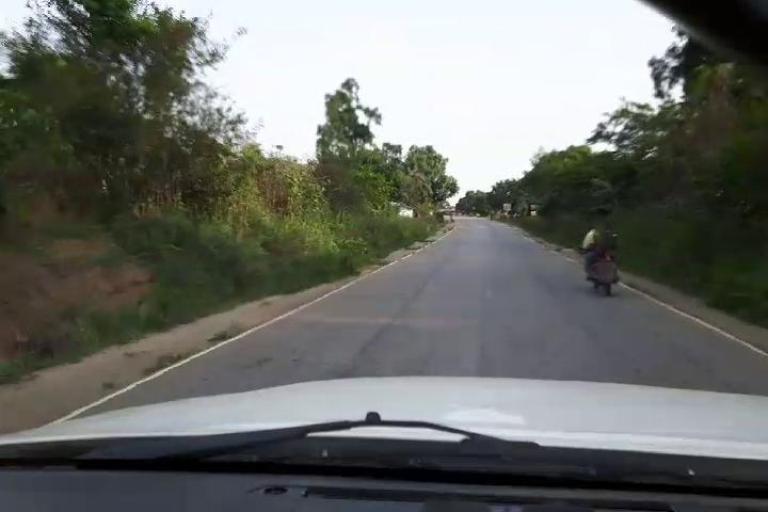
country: SL
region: Eastern Province
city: Blama
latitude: 7.9173
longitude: -11.4234
